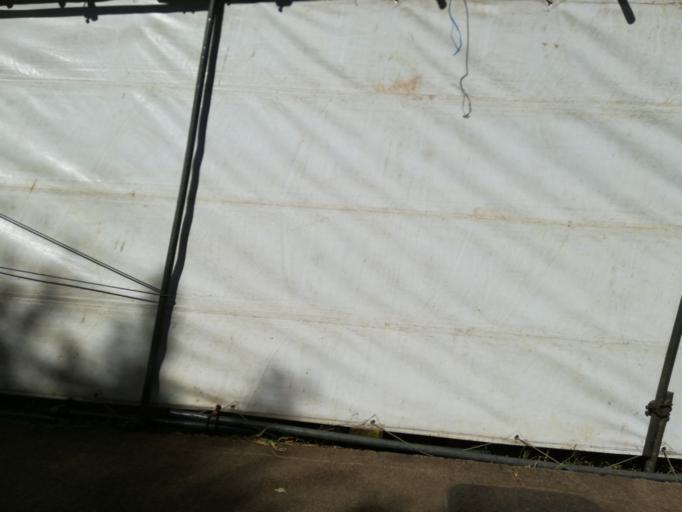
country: MU
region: Moka
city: Pailles
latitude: -20.1915
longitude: 57.4789
